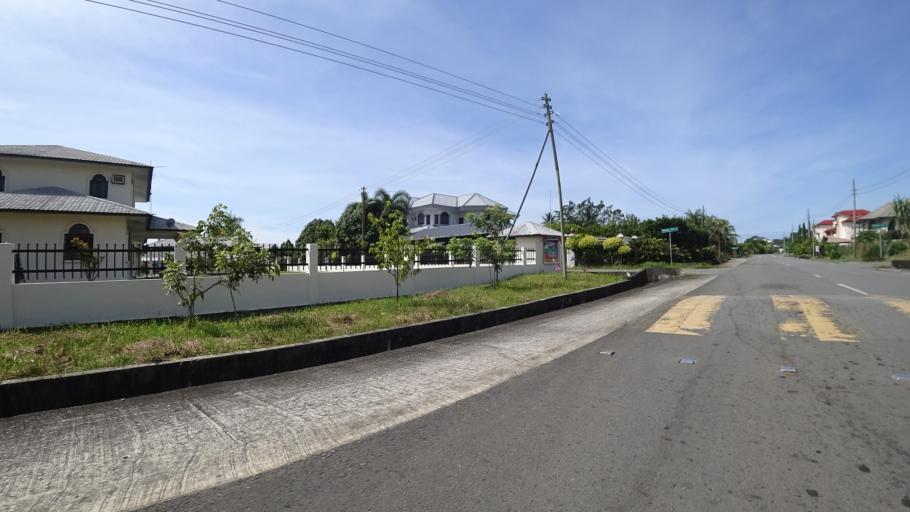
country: BN
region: Brunei and Muara
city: Bandar Seri Begawan
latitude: 4.8848
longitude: 114.8490
